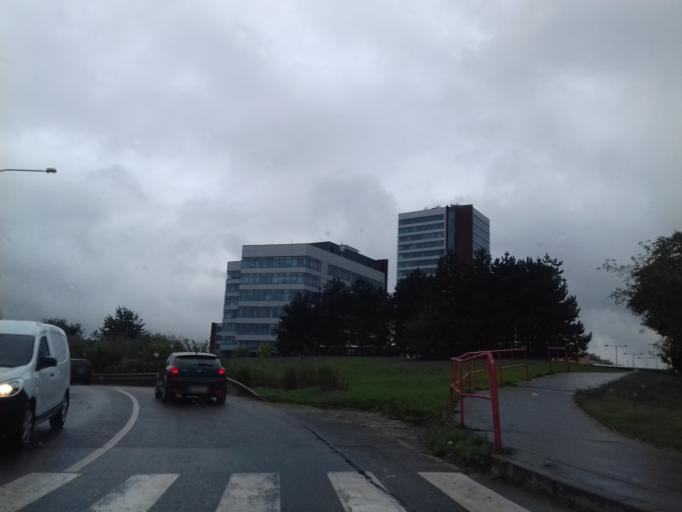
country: CZ
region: Praha
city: Branik
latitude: 50.0516
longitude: 14.3553
